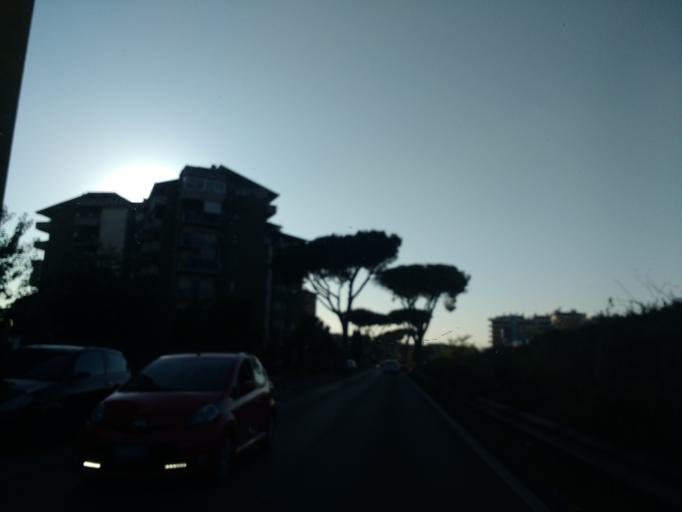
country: IT
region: Latium
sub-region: Citta metropolitana di Roma Capitale
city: Vitinia
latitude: 41.7688
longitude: 12.3766
